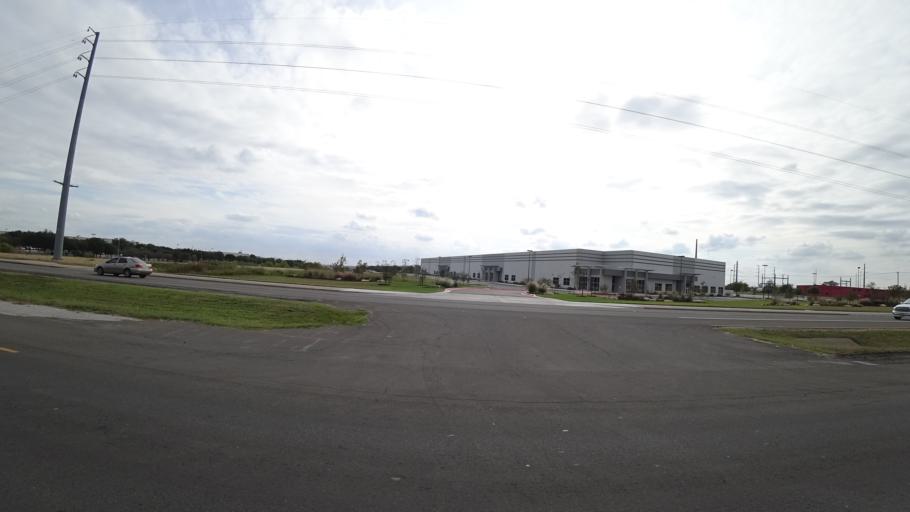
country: US
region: Texas
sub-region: Travis County
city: Wells Branch
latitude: 30.4201
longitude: -97.6622
